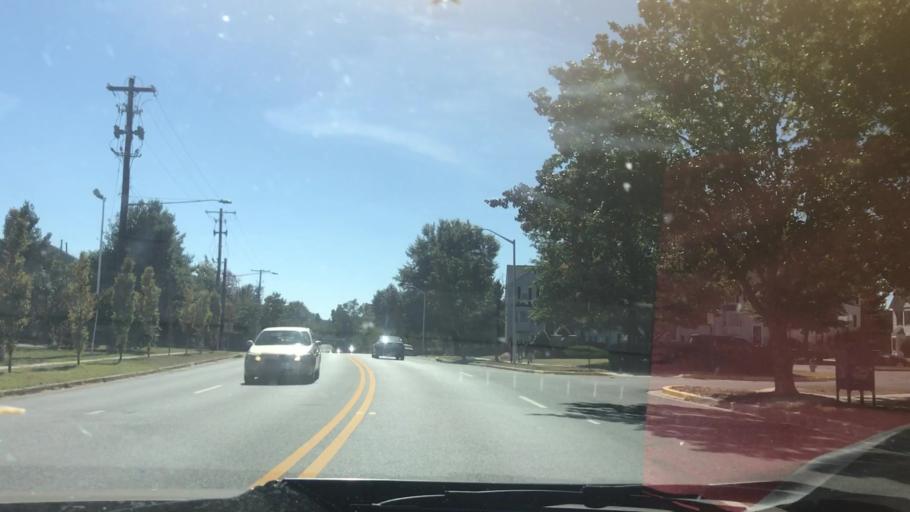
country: US
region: Maryland
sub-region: Prince George's County
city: Suitland
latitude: 38.8414
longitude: -76.9095
